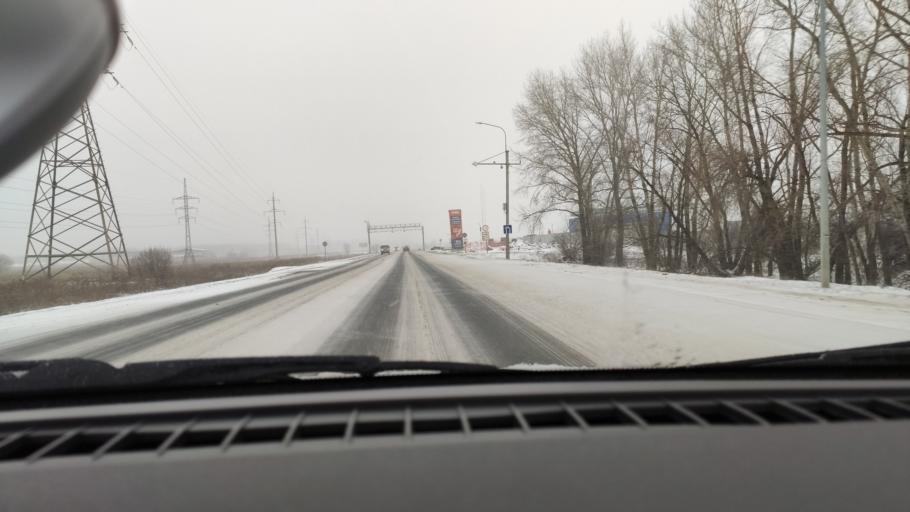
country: RU
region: Samara
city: Samara
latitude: 53.1309
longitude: 50.1531
